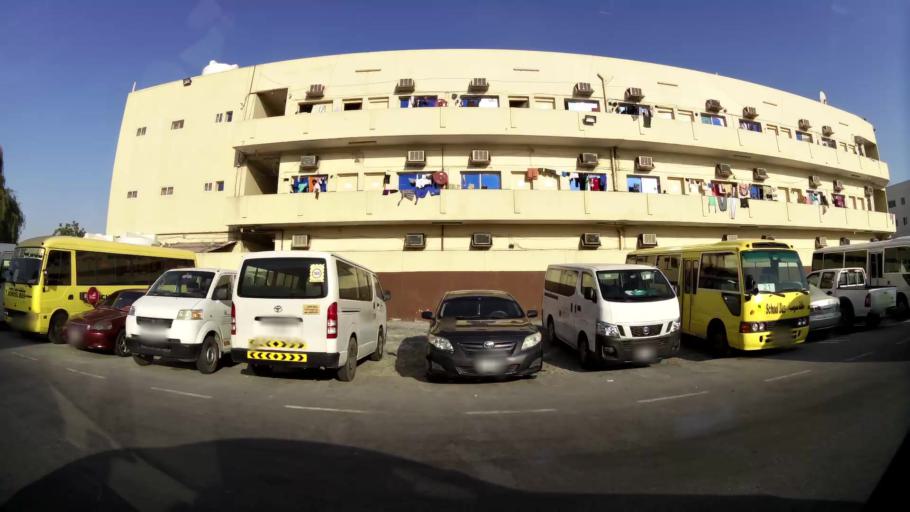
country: AE
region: Dubai
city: Dubai
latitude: 25.1317
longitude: 55.2352
